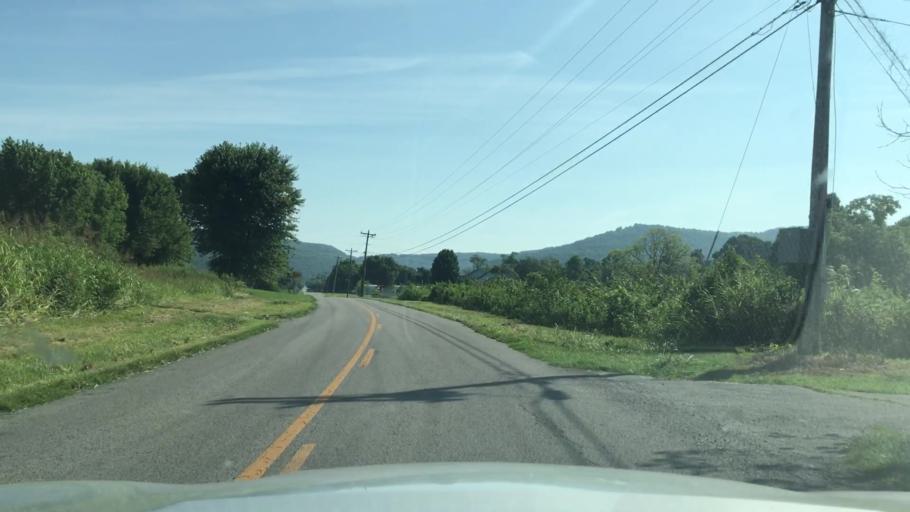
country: US
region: Kentucky
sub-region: Clinton County
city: Albany
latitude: 36.6917
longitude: -85.0488
